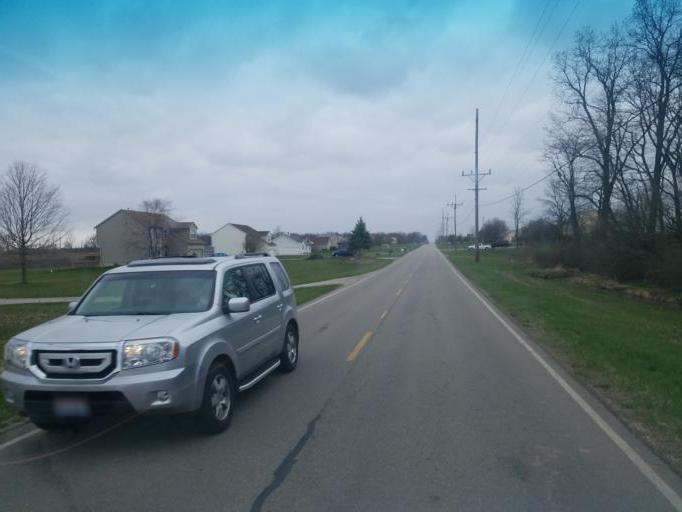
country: US
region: Ohio
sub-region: Marion County
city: Marion
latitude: 40.5261
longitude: -83.1508
